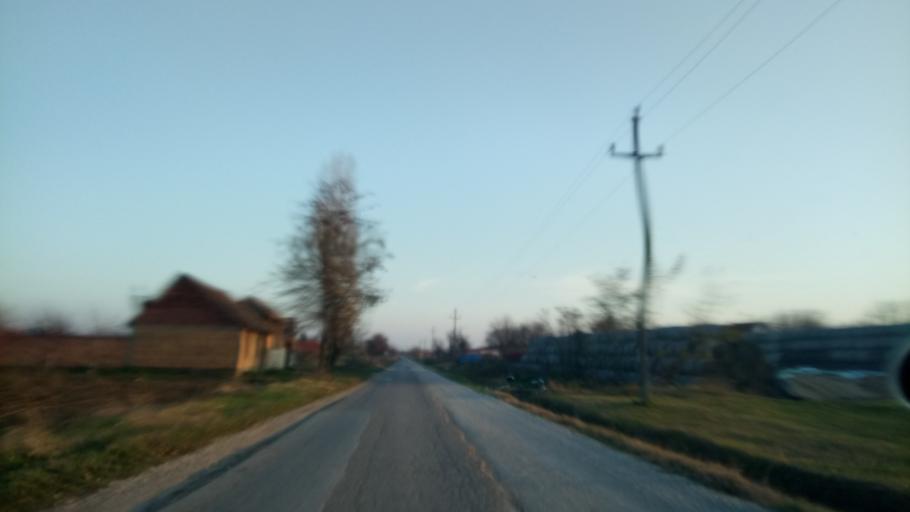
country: RS
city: Novi Slankamen
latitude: 45.1316
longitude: 20.2549
